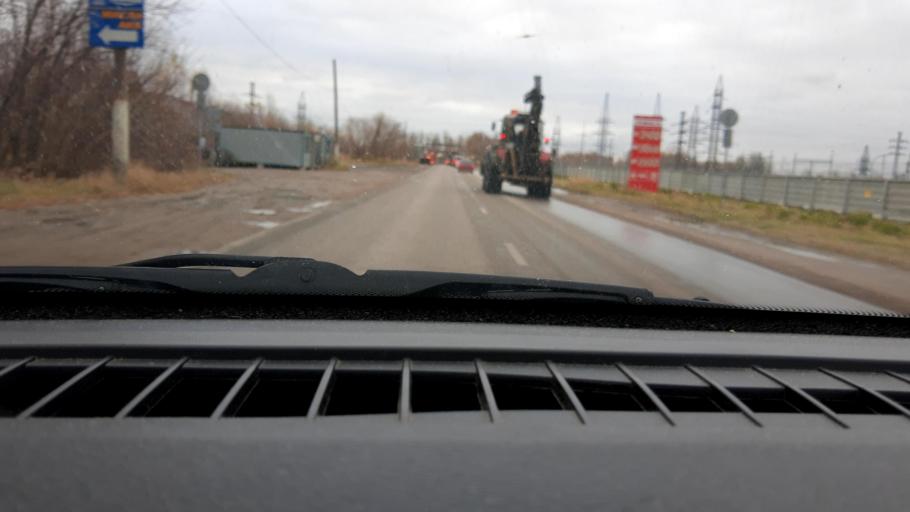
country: RU
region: Nizjnij Novgorod
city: Kstovo
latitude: 56.1185
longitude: 44.1466
